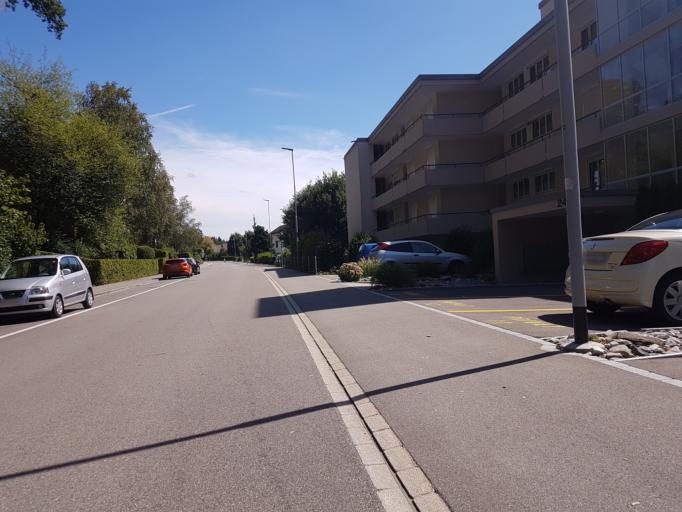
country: CH
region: Zurich
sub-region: Bezirk Pfaeffikon
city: Effretikon / Watt
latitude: 47.4274
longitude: 8.6982
